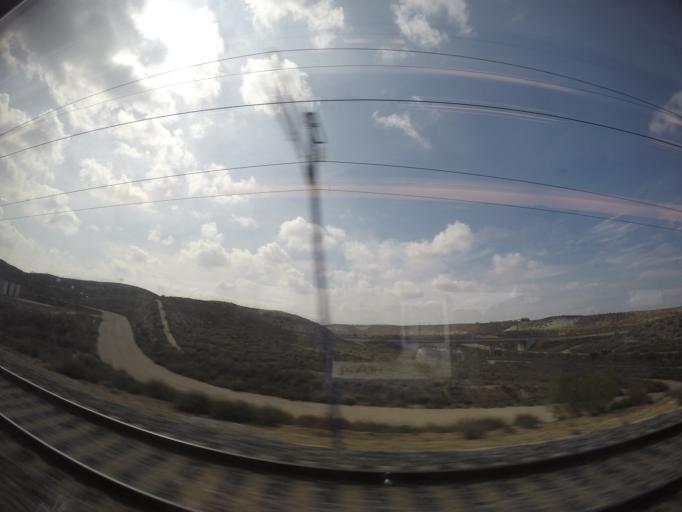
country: ES
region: Aragon
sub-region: Provincia de Zaragoza
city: El Burgo de Ebro
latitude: 41.5582
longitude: -0.7670
